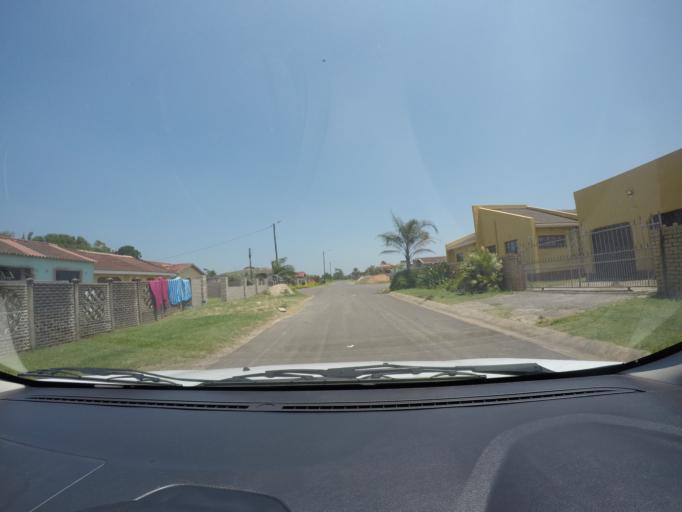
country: ZA
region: KwaZulu-Natal
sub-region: uThungulu District Municipality
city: eSikhawini
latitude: -28.8884
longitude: 31.8853
